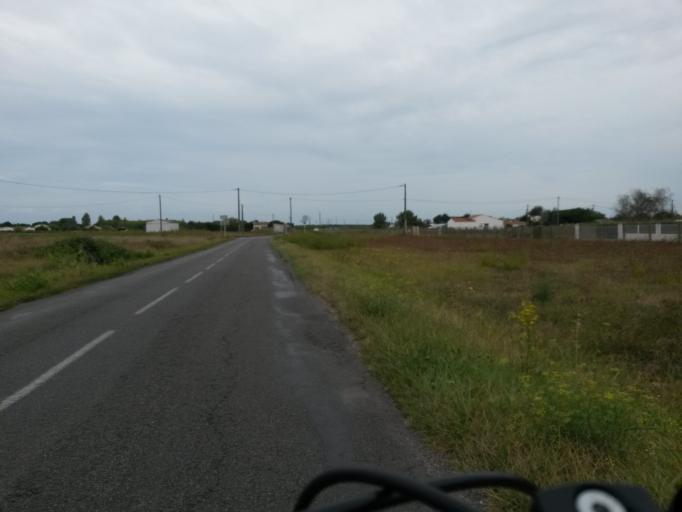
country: FR
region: Poitou-Charentes
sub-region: Departement de la Charente-Maritime
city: Dolus-d'Oleron
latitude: 45.9330
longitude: -1.3340
